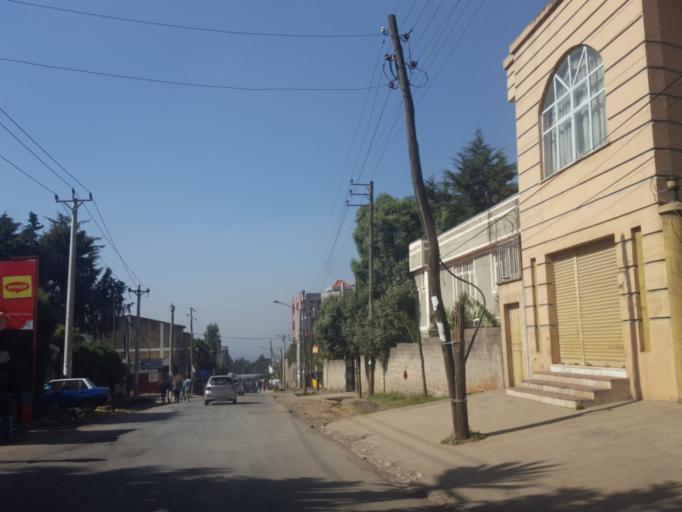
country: ET
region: Adis Abeba
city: Addis Ababa
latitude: 9.0510
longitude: 38.7282
